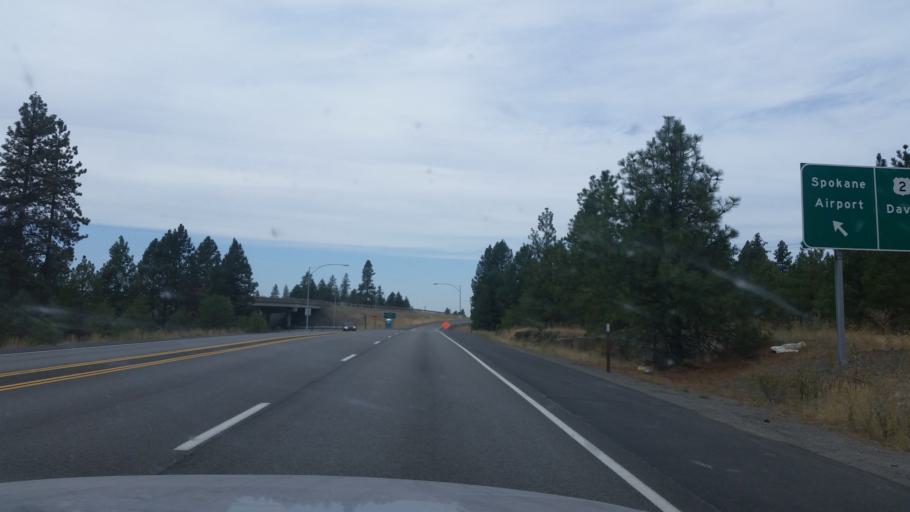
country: US
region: Washington
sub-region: Spokane County
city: Spokane
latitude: 47.6430
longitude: -117.4983
